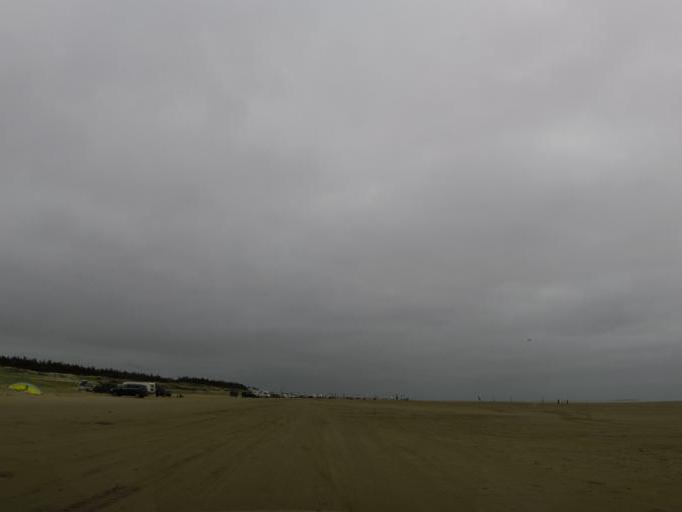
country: DE
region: Schleswig-Holstein
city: List
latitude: 55.0832
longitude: 8.5149
